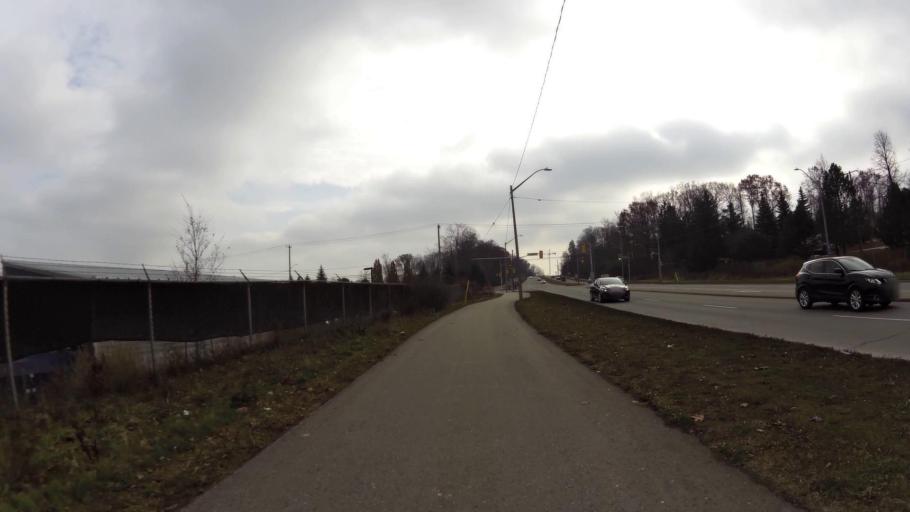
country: CA
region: Ontario
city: Kitchener
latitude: 43.4243
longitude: -80.4765
